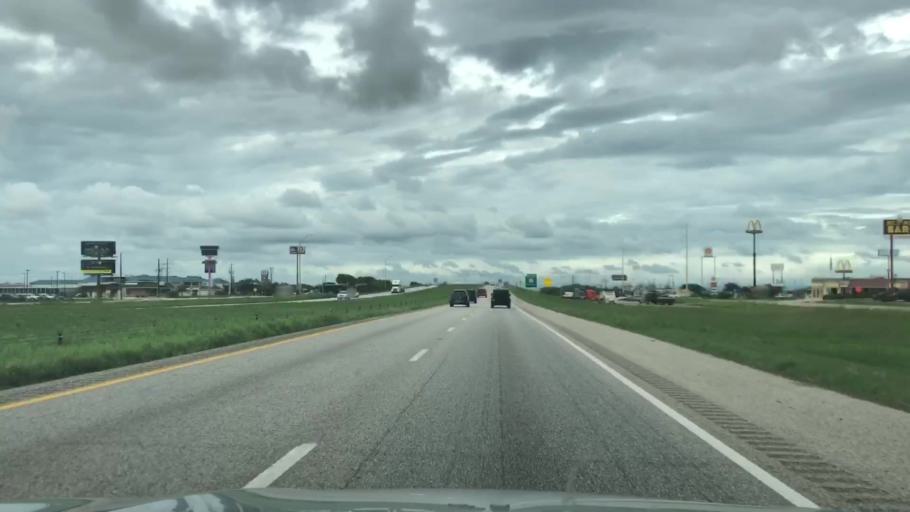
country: US
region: Texas
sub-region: Guadalupe County
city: Seguin
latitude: 29.5811
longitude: -97.9968
